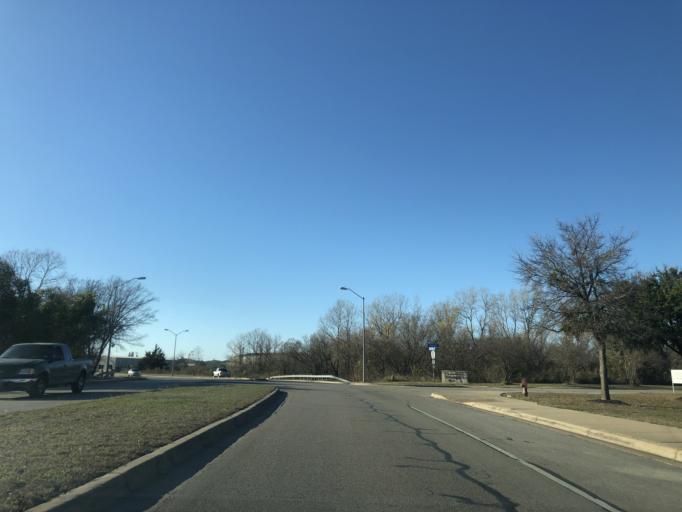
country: US
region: Texas
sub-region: Travis County
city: Windemere
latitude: 30.4676
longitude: -97.6558
